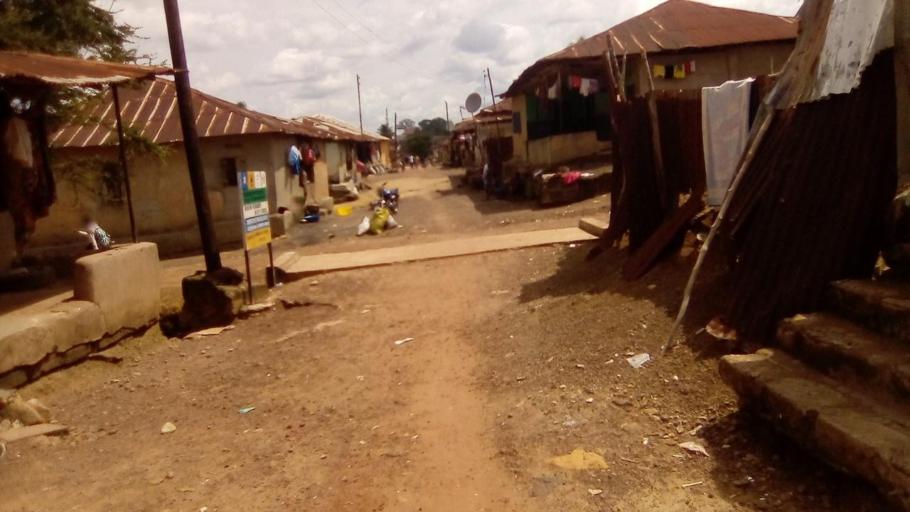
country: SL
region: Southern Province
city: Bo
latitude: 7.9669
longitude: -11.7332
